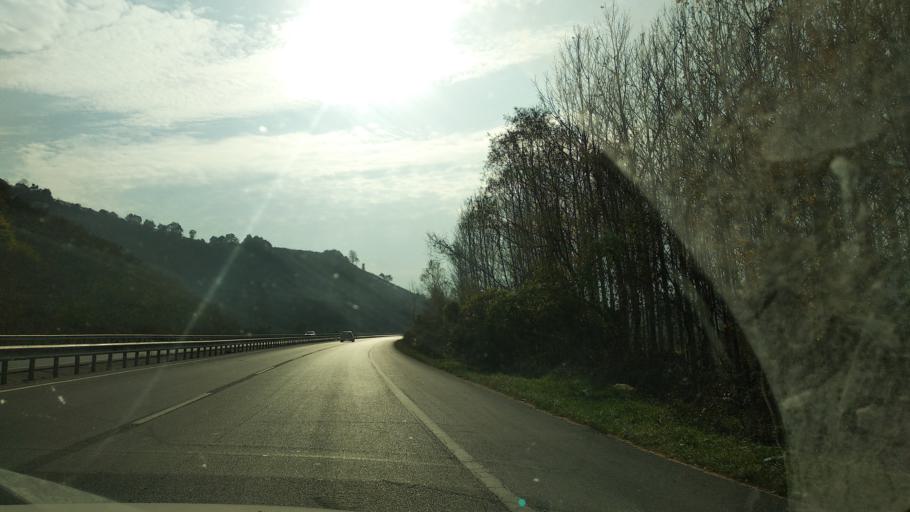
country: TR
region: Sakarya
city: Karasu
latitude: 41.0669
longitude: 30.6432
